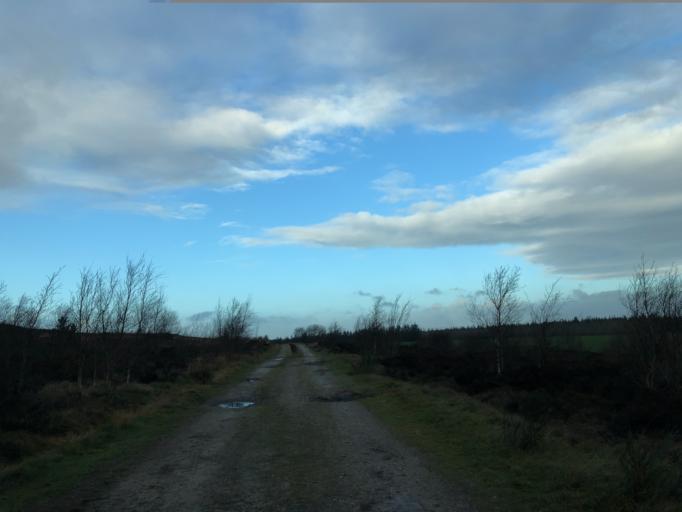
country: DK
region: Central Jutland
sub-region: Ringkobing-Skjern Kommune
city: Videbaek
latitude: 56.1849
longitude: 8.6612
